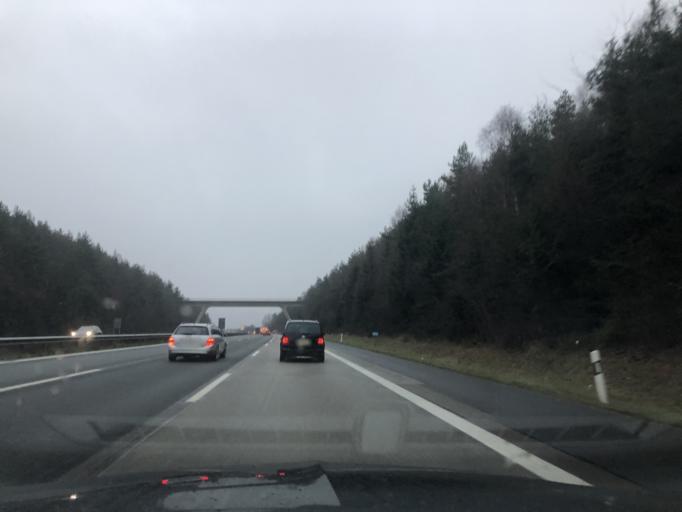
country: DE
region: Rheinland-Pfalz
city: Birkheim
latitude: 50.0994
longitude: 7.6033
